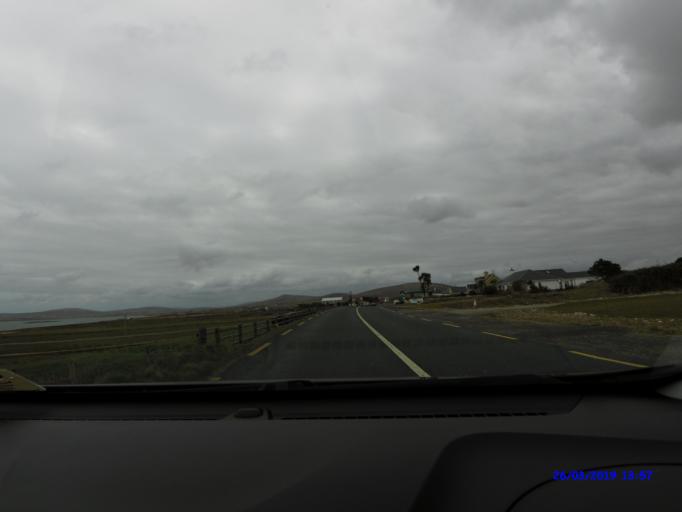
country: IE
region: Connaught
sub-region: Maigh Eo
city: Belmullet
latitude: 54.2085
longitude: -9.9372
